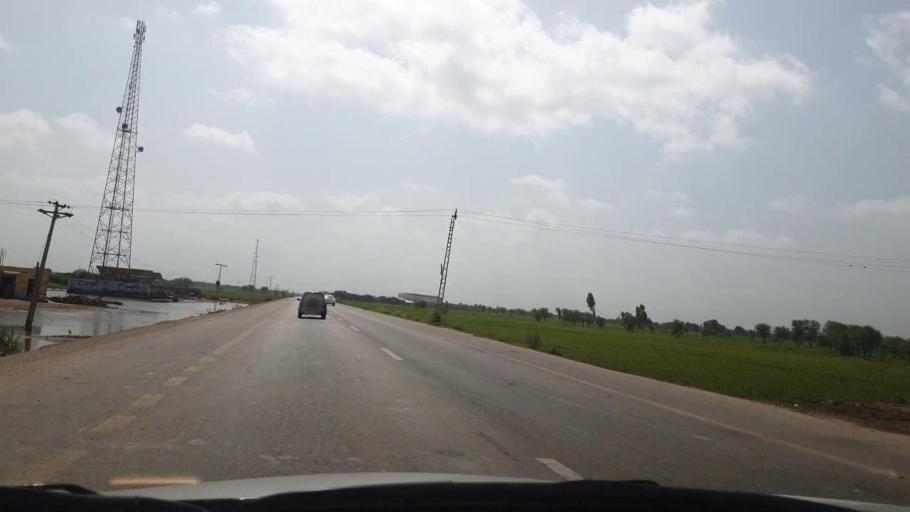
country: PK
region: Sindh
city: Matli
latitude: 24.9405
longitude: 68.7040
